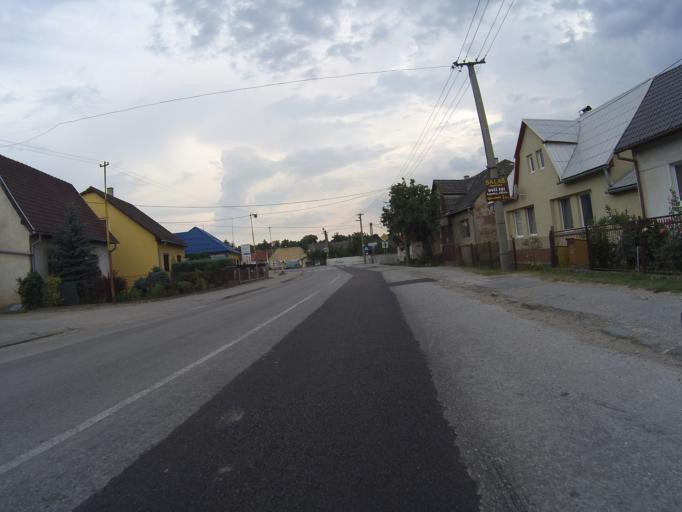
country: SK
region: Nitriansky
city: Ilava
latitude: 49.0384
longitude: 18.2881
